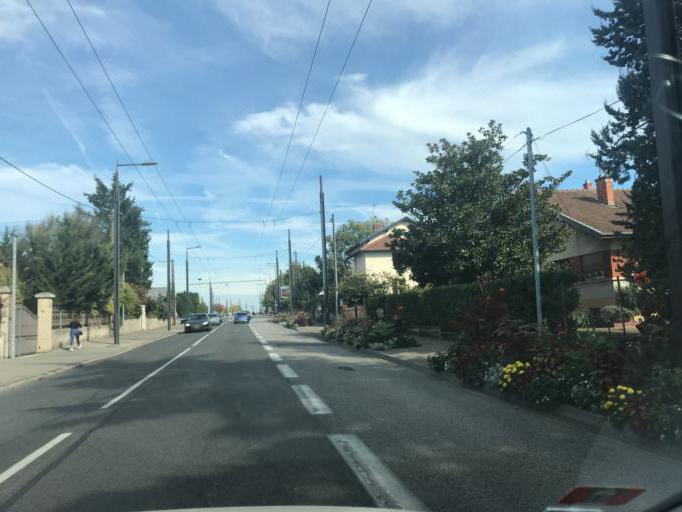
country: FR
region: Rhone-Alpes
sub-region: Departement du Rhone
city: Caluire-et-Cuire
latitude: 45.8020
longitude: 4.8567
